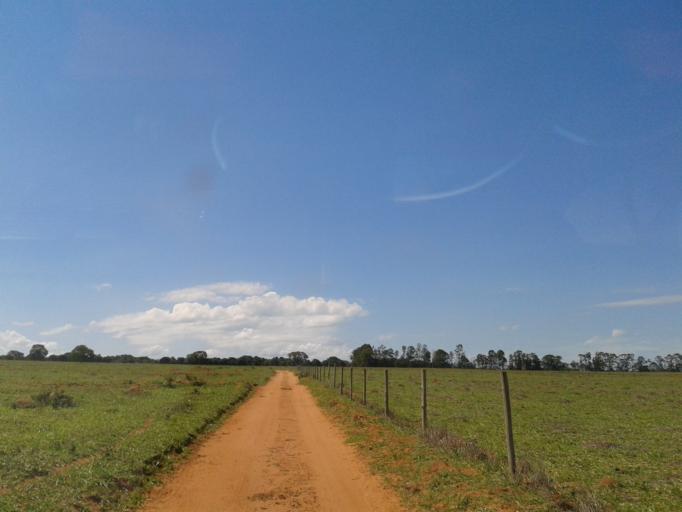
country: BR
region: Minas Gerais
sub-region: Centralina
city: Centralina
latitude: -18.7132
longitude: -49.1561
